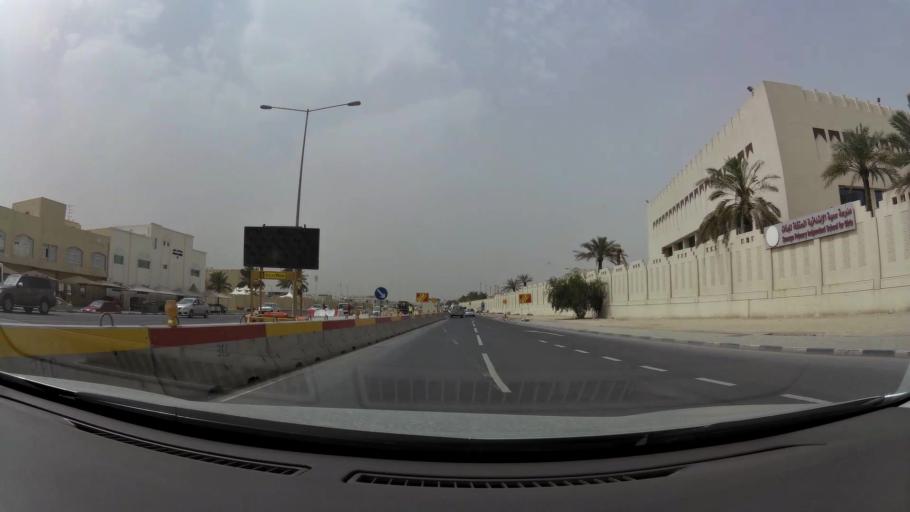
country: QA
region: Baladiyat ad Dawhah
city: Doha
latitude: 25.2666
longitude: 51.5119
